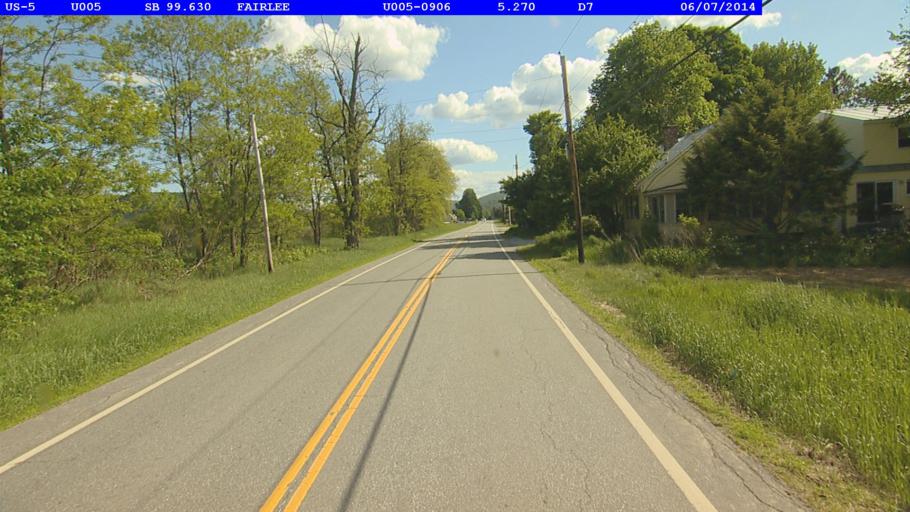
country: US
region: New Hampshire
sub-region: Grafton County
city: Orford
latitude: 43.9328
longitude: -72.1205
